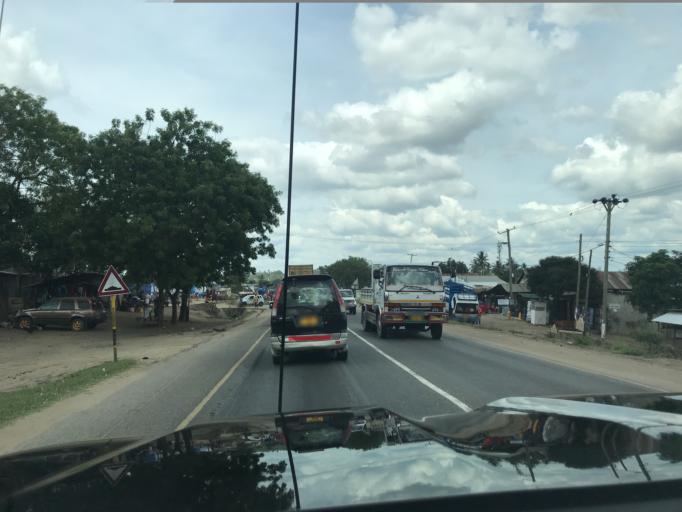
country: TZ
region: Pwani
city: Kibaha
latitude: -6.7650
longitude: 38.9543
